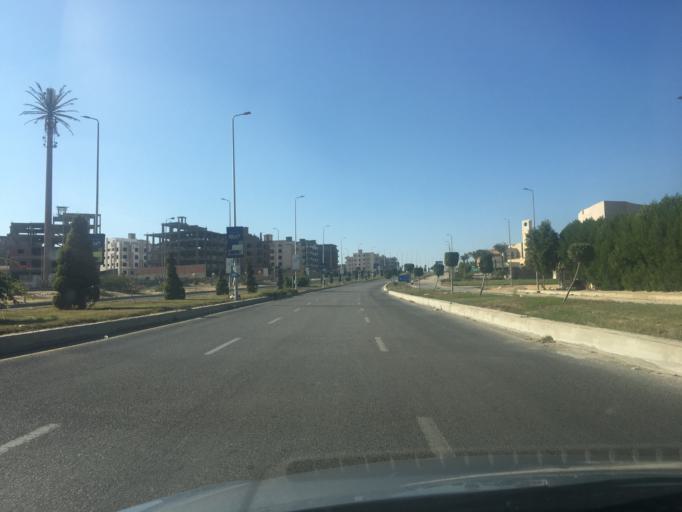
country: EG
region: Al Jizah
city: Awsim
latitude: 30.0197
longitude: 30.9881
